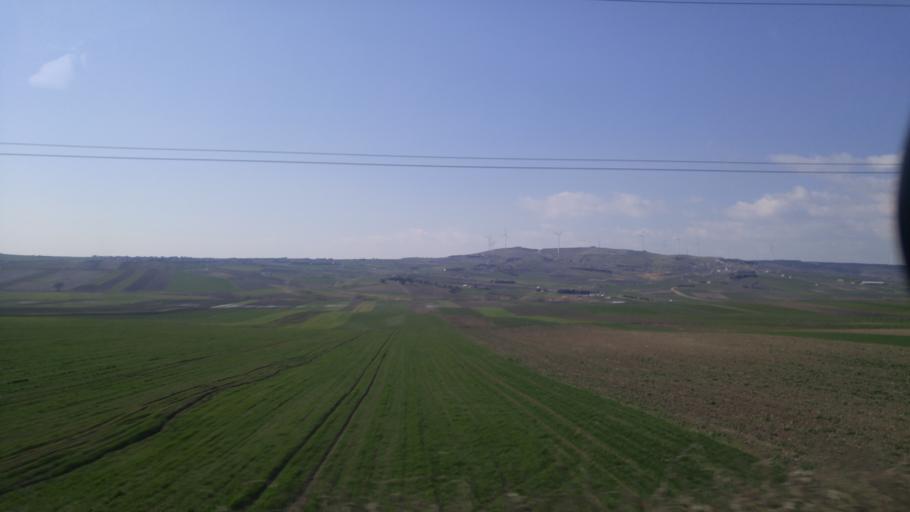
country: TR
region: Istanbul
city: Canta
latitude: 41.1023
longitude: 28.1110
